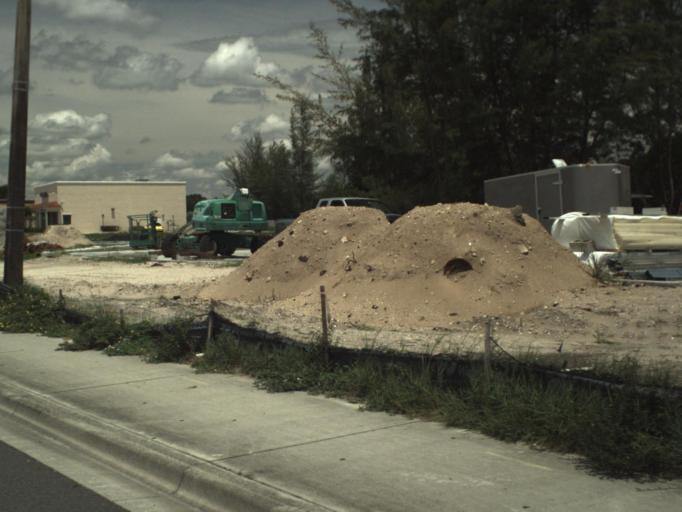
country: US
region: Florida
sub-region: Palm Beach County
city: Mangonia Park
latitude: 26.7814
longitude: -80.0839
